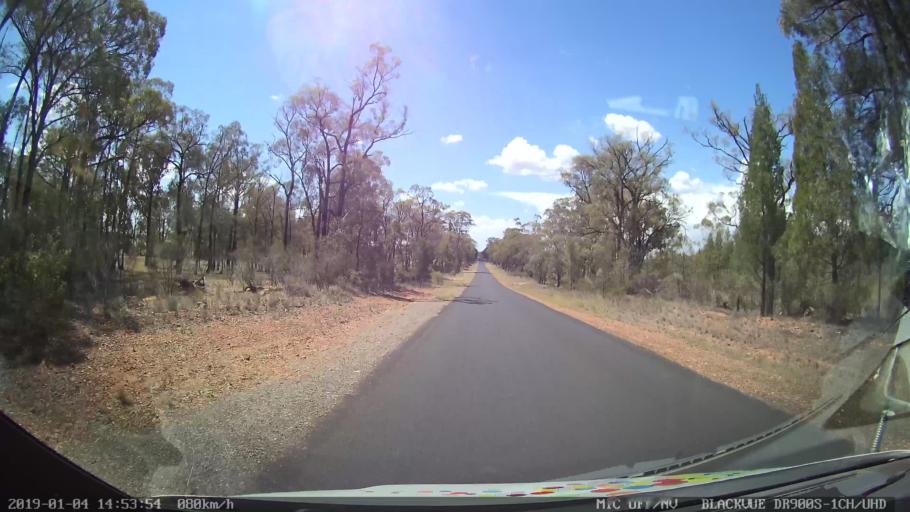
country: AU
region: New South Wales
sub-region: Dubbo Municipality
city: Dubbo
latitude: -31.9976
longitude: 148.6528
